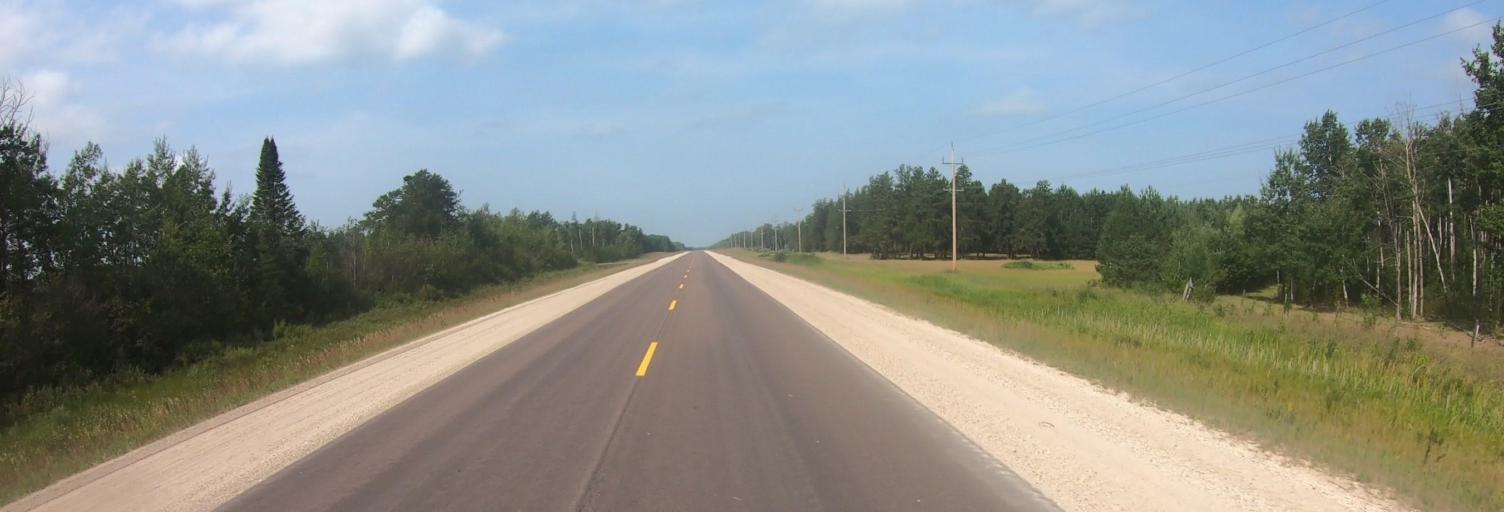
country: CA
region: Manitoba
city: La Broquerie
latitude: 49.2669
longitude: -96.4265
